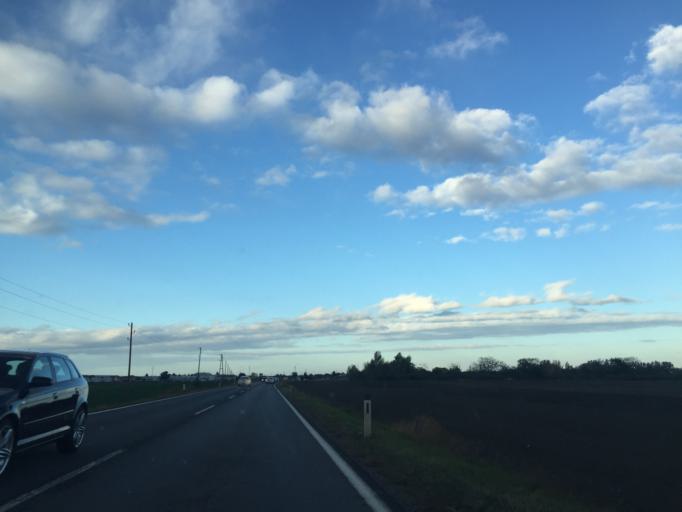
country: AT
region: Lower Austria
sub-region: Politischer Bezirk Wien-Umgebung
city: Gerasdorf bei Wien
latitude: 48.2841
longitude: 16.4614
